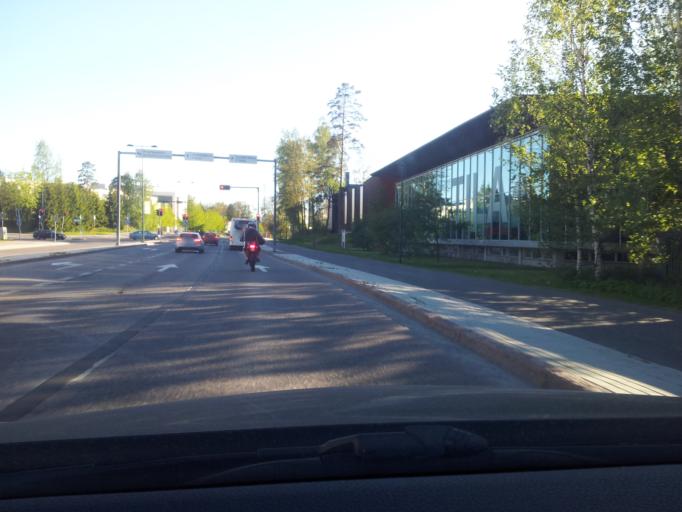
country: FI
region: Uusimaa
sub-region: Helsinki
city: Koukkuniemi
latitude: 60.1650
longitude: 24.7258
